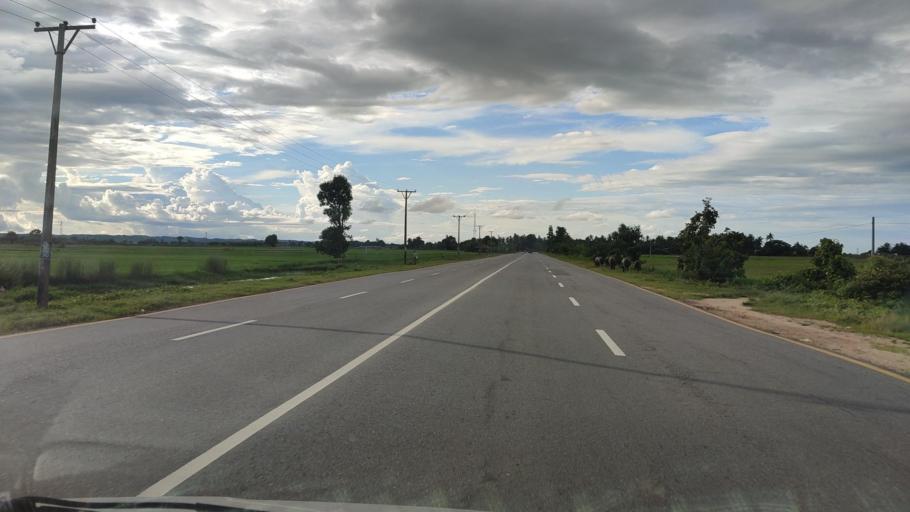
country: MM
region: Bago
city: Taungoo
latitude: 19.2159
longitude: 96.2975
